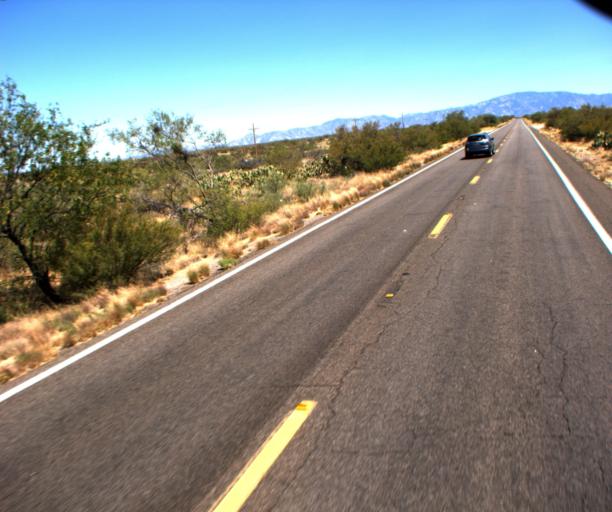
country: US
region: Arizona
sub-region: Pima County
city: Catalina
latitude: 32.6420
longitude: -111.0160
